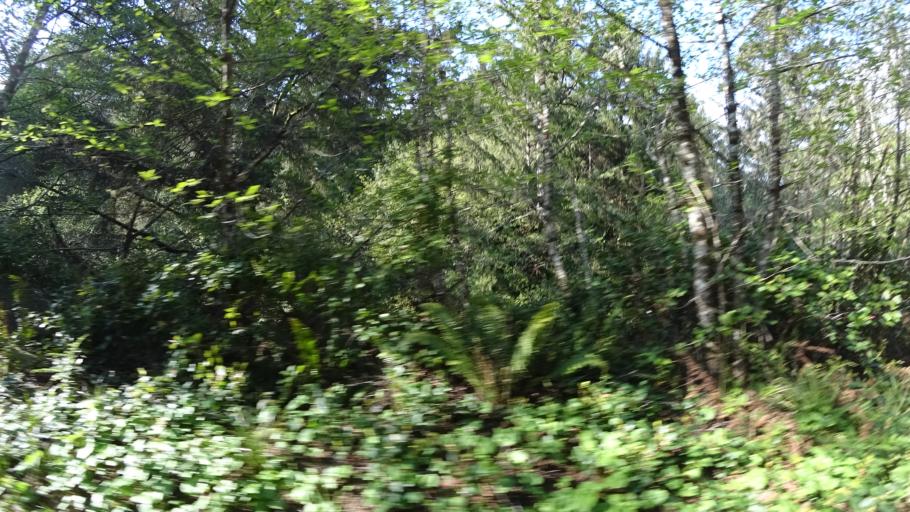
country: US
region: Oregon
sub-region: Douglas County
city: Reedsport
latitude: 43.7488
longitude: -124.1772
